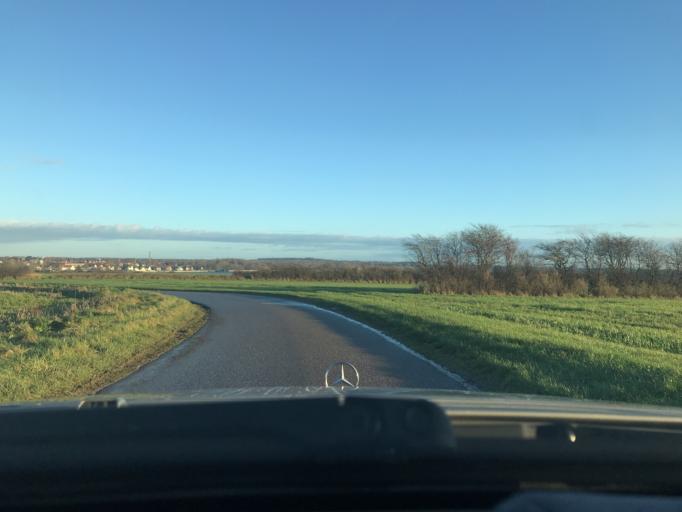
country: DK
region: South Denmark
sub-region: Sonderborg Kommune
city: Dybbol
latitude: 54.9019
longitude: 9.7643
